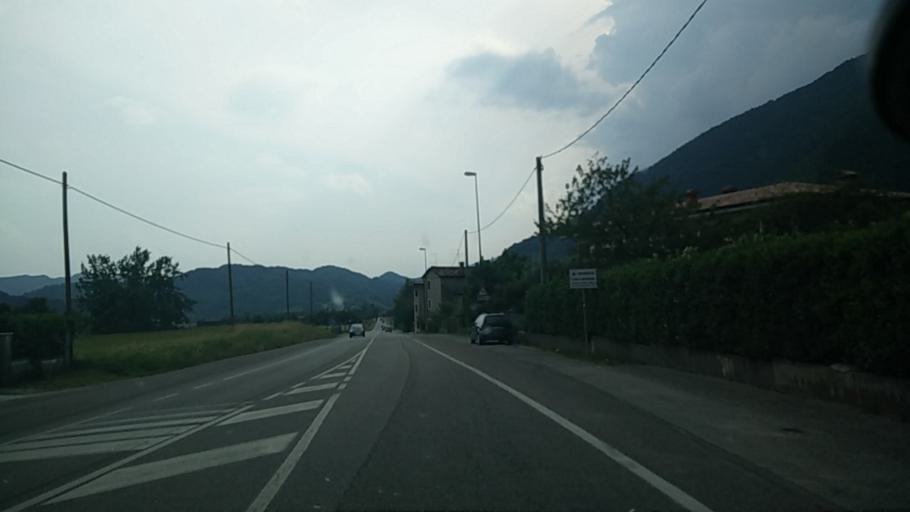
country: IT
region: Veneto
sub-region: Provincia di Treviso
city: Cison di Valmarino
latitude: 45.9654
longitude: 12.1348
